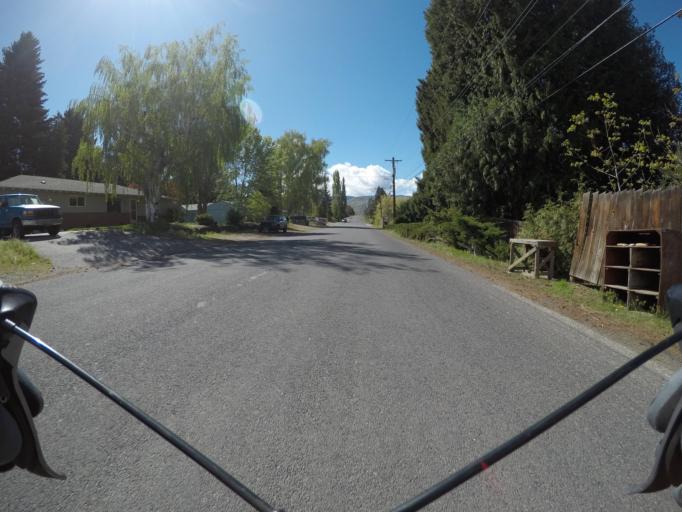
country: US
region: Washington
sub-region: Douglas County
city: East Wenatchee Bench
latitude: 47.4122
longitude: -120.2711
